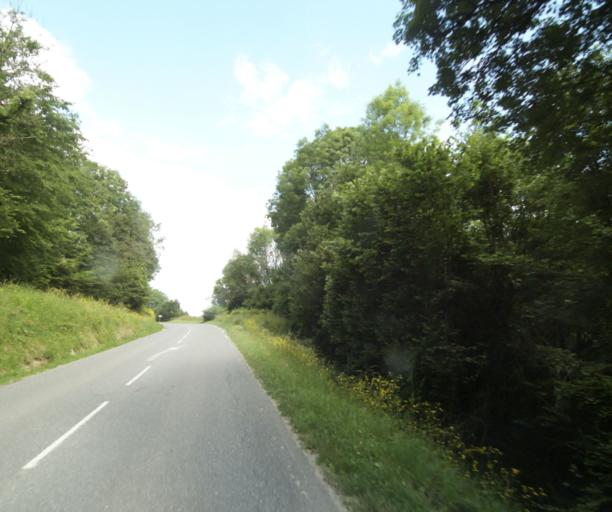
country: FR
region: Rhone-Alpes
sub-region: Departement de la Haute-Savoie
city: Allinges
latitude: 46.3358
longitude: 6.4742
